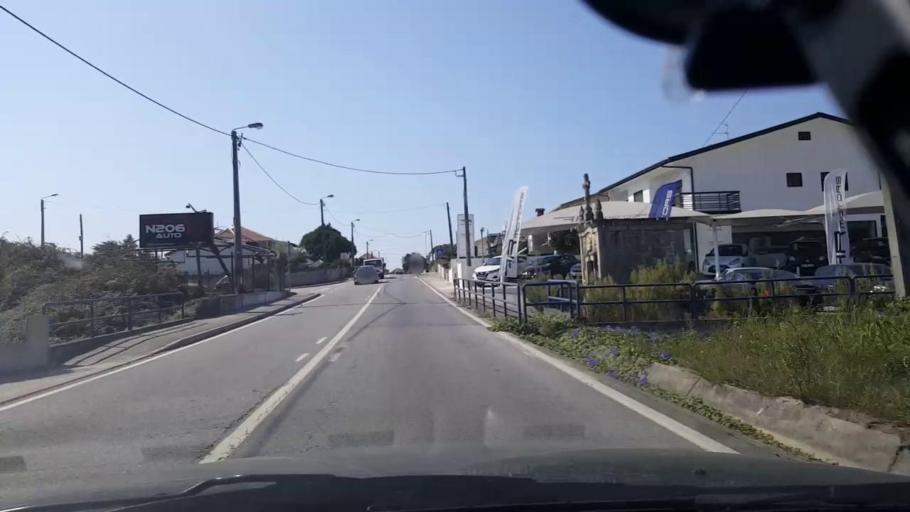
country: PT
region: Porto
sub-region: Povoa de Varzim
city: Pedroso
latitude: 41.3904
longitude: -8.7034
